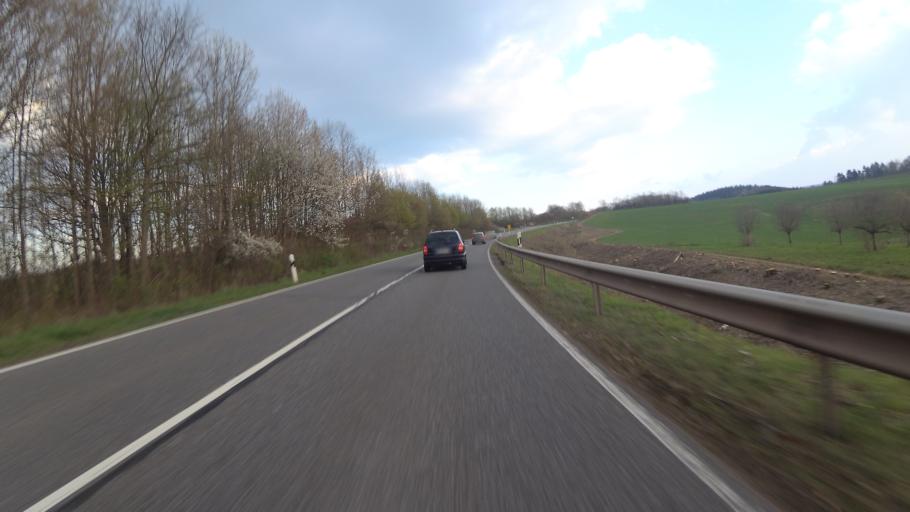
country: DE
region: Rheinland-Pfalz
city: Monzelfeld
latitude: 49.8905
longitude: 7.0599
